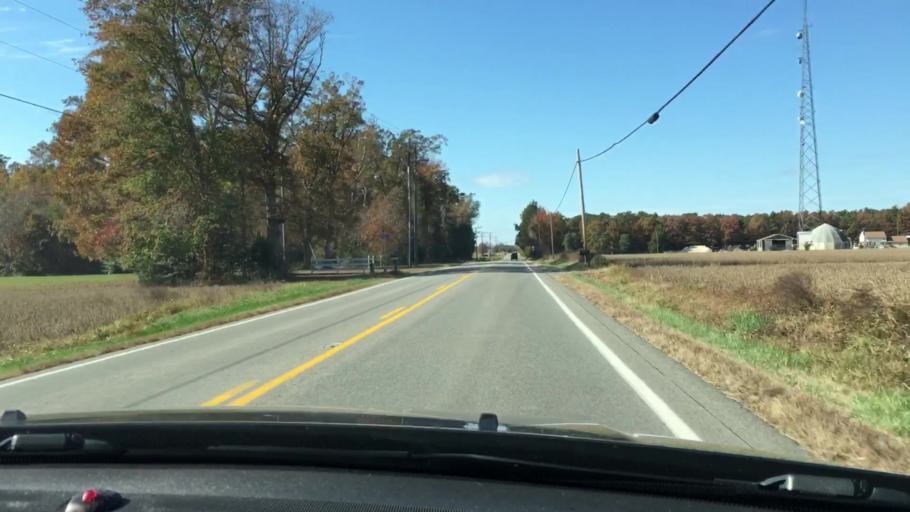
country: US
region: Virginia
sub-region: King William County
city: Central Garage
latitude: 37.7198
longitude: -77.0786
